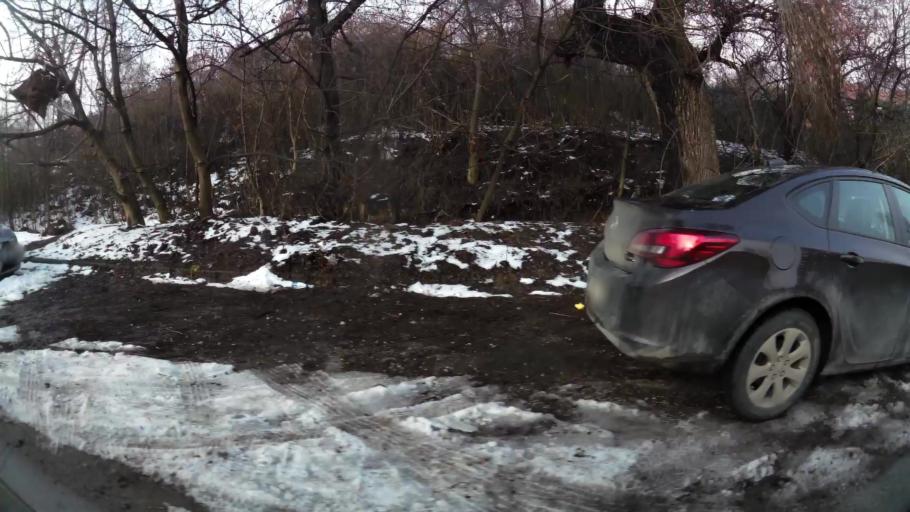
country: BG
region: Sofia-Capital
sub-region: Stolichna Obshtina
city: Sofia
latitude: 42.6572
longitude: 23.2625
